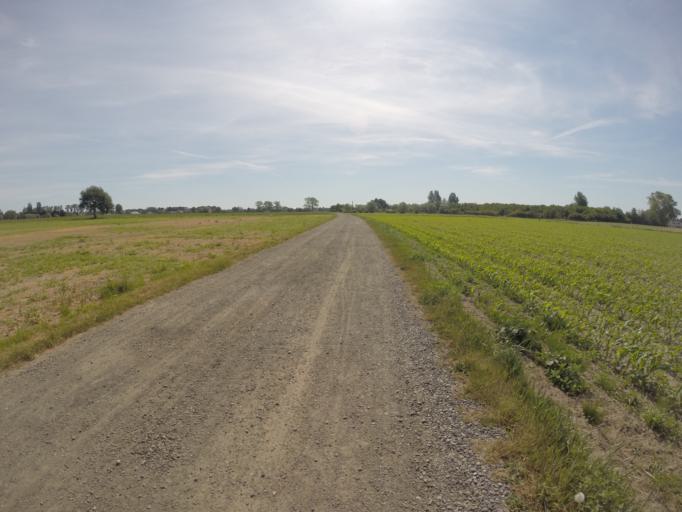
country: BE
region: Flanders
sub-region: Provincie West-Vlaanderen
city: Beernem
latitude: 51.1773
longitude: 3.3282
